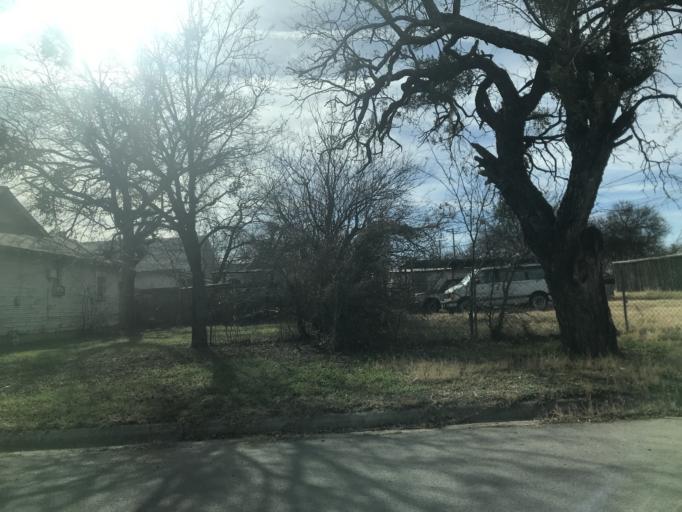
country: US
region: Texas
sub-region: Taylor County
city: Abilene
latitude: 32.4446
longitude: -99.7370
